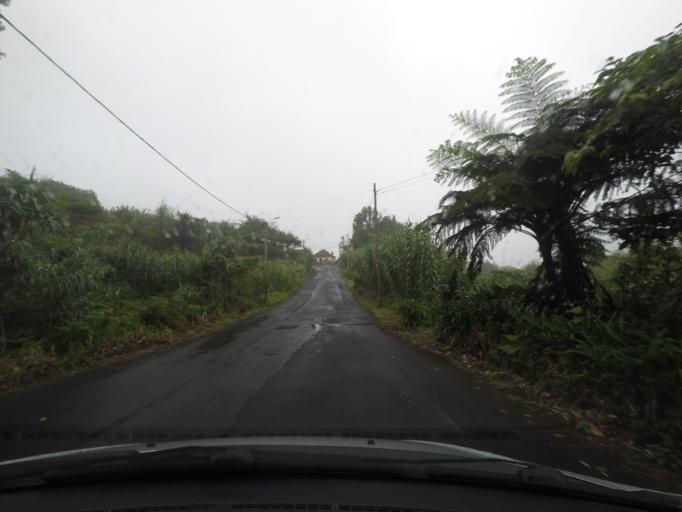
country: PT
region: Madeira
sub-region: Santana
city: Santana
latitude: 32.7943
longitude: -16.8706
